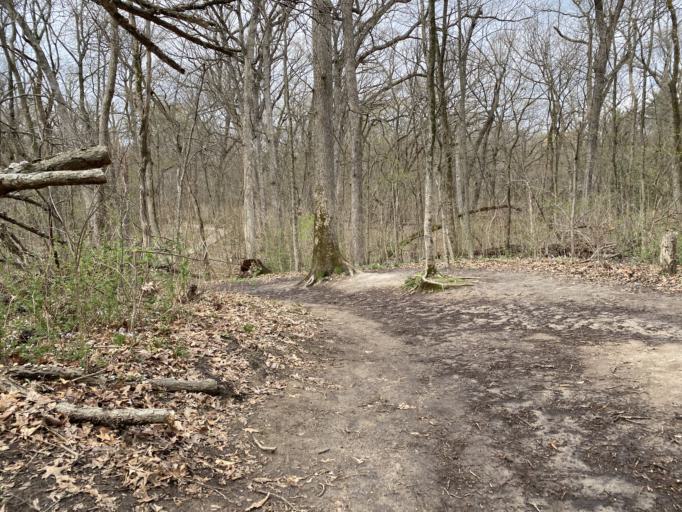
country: US
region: Illinois
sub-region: LaSalle County
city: Deer Park
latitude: 41.3166
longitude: -88.9853
